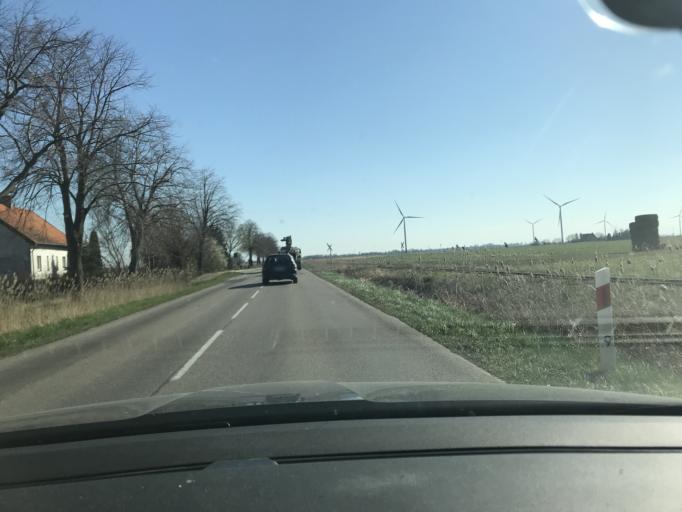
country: PL
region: Pomeranian Voivodeship
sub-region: Powiat nowodworski
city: Nowy Dwor Gdanski
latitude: 54.2633
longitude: 19.1360
